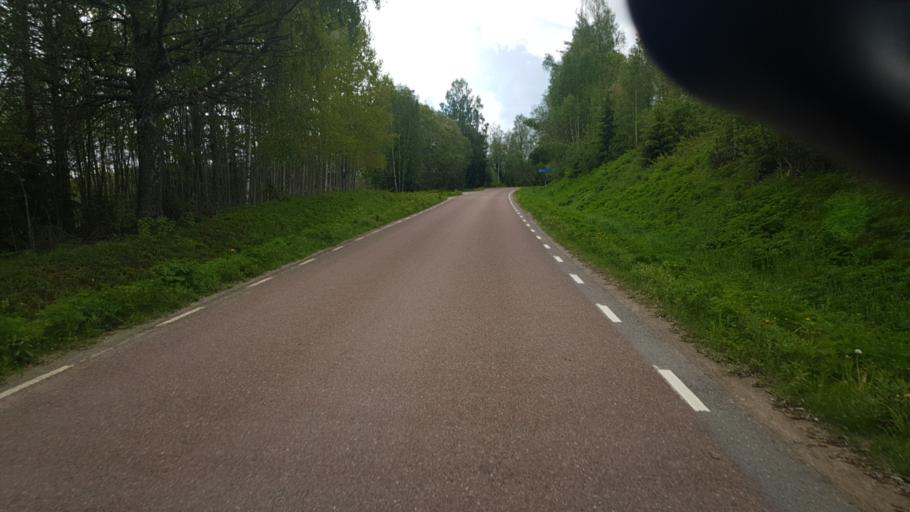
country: NO
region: Ostfold
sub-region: Romskog
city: Romskog
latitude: 59.7506
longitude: 12.0542
